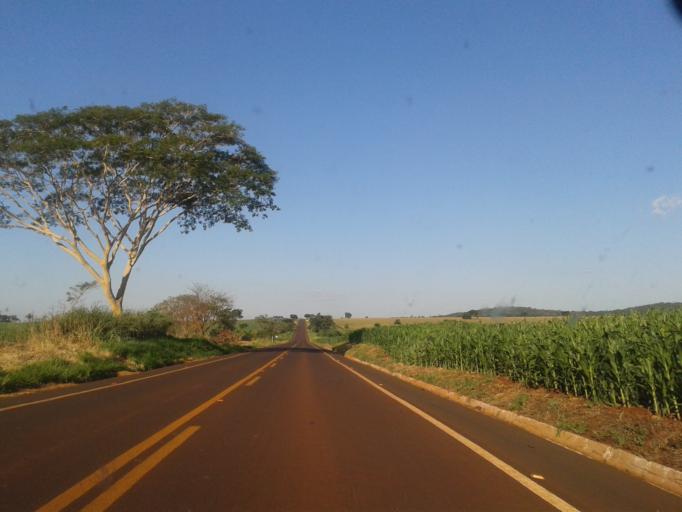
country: BR
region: Minas Gerais
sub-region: Capinopolis
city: Capinopolis
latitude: -18.7121
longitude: -49.8198
